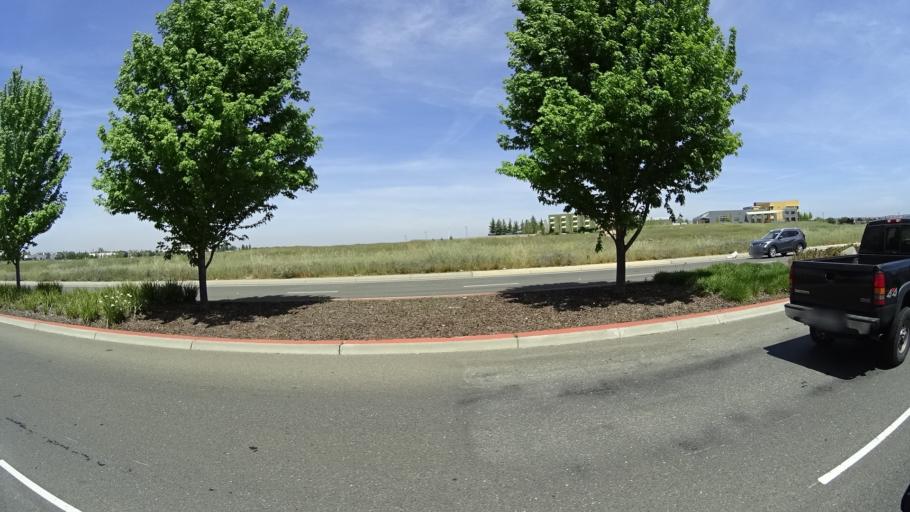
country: US
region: California
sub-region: Placer County
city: Roseville
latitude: 38.8168
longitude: -121.2957
